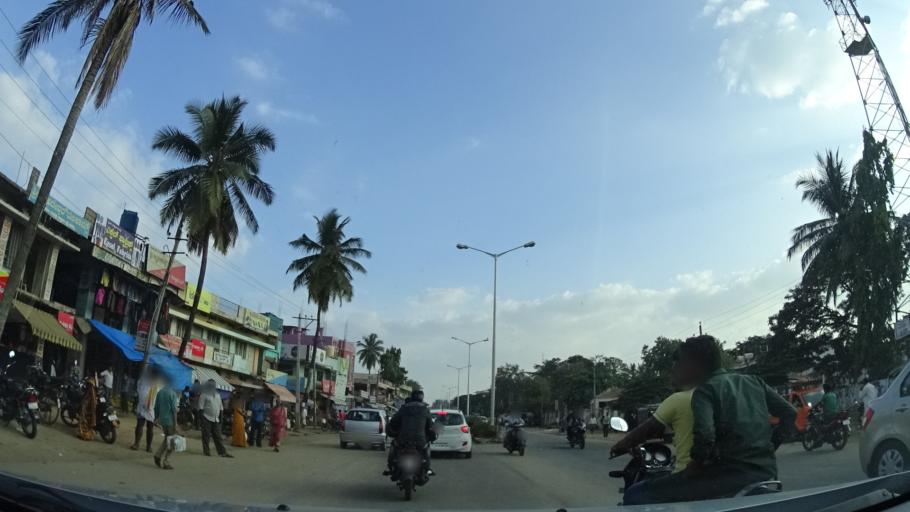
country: IN
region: Karnataka
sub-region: Mandya
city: Malavalli
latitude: 12.3858
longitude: 77.0599
